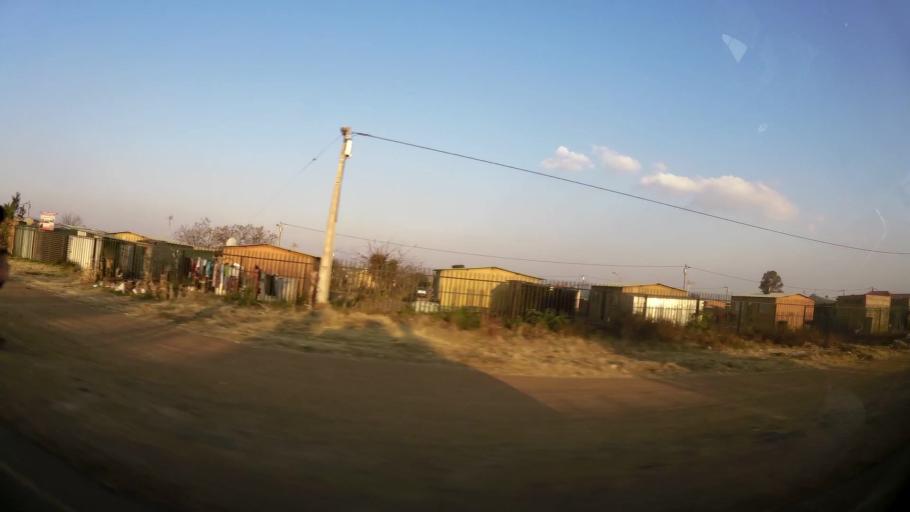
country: ZA
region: Gauteng
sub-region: Ekurhuleni Metropolitan Municipality
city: Benoni
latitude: -26.1537
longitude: 28.3792
